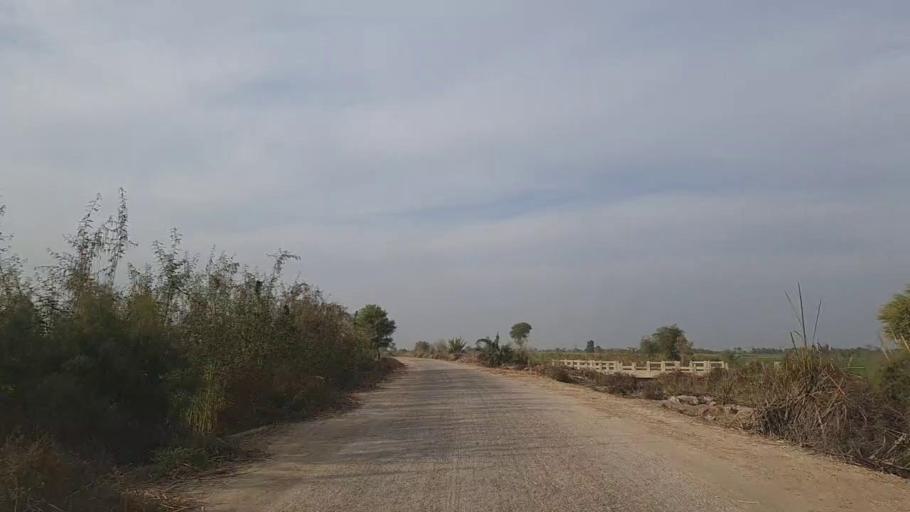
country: PK
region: Sindh
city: Daur
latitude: 26.4862
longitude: 68.4634
